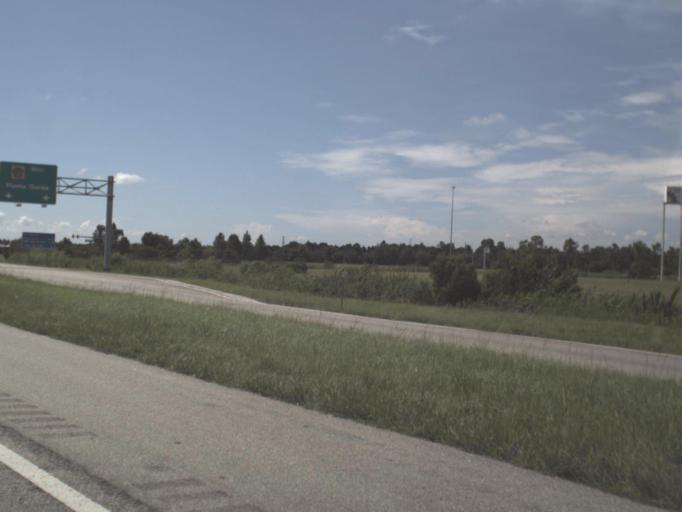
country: US
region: Florida
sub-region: Charlotte County
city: Charlotte Park
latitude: 26.8979
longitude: -82.0055
